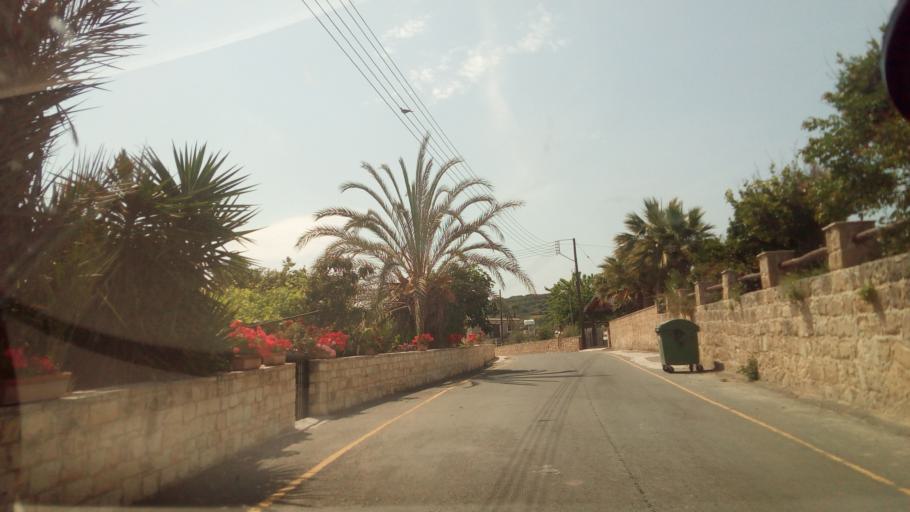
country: CY
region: Pafos
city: Polis
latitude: 34.9544
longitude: 32.4510
